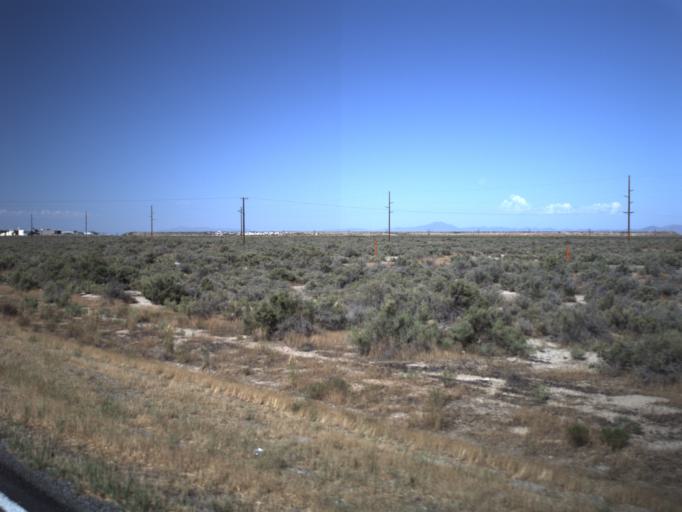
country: US
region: Utah
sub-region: Millard County
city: Delta
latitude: 39.4784
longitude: -112.4156
